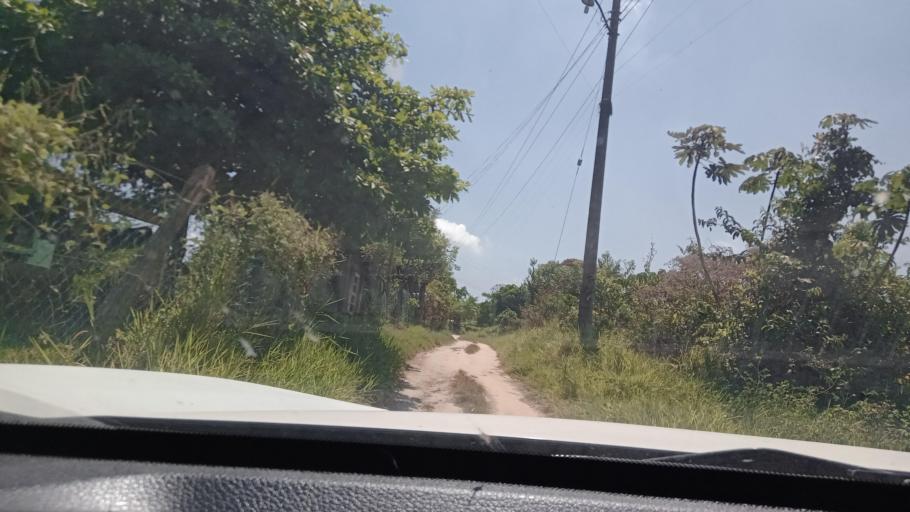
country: MX
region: Veracruz
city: Las Choapas
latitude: 17.7556
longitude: -94.1145
